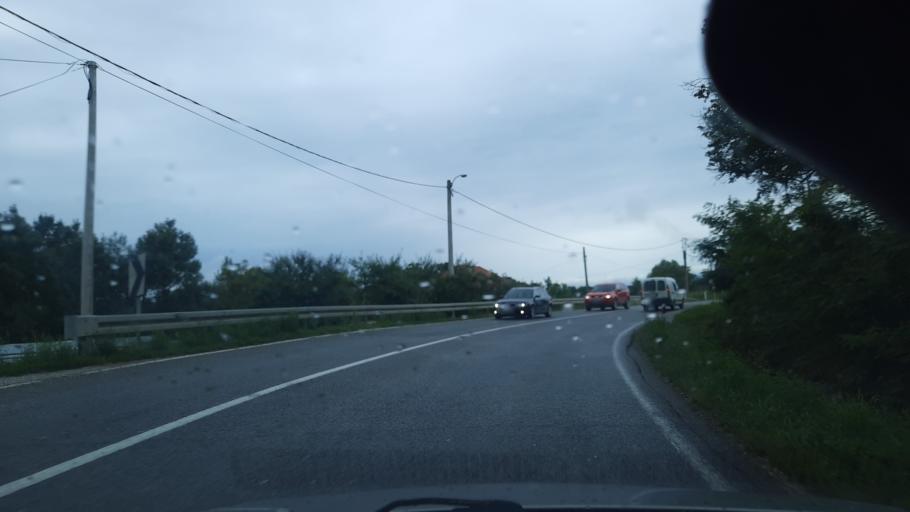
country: RS
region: Central Serbia
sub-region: Raski Okrug
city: Kraljevo
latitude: 43.7795
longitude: 20.7956
